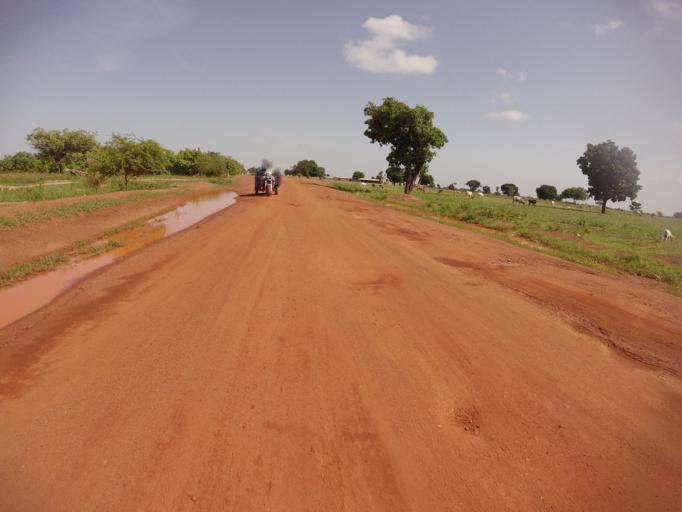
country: GH
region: Upper East
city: Bawku
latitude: 11.0096
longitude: -0.2011
